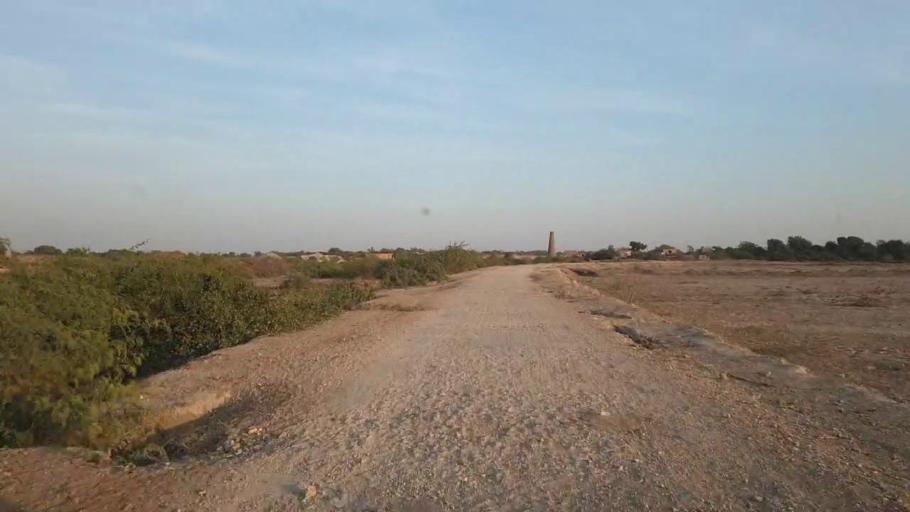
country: PK
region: Sindh
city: Chambar
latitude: 25.2817
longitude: 68.8302
